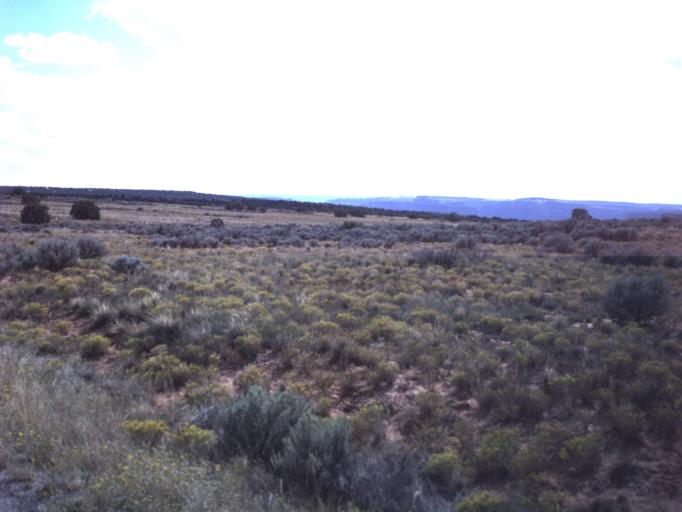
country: US
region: Utah
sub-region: Grand County
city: Moab
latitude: 38.5147
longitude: -109.7297
